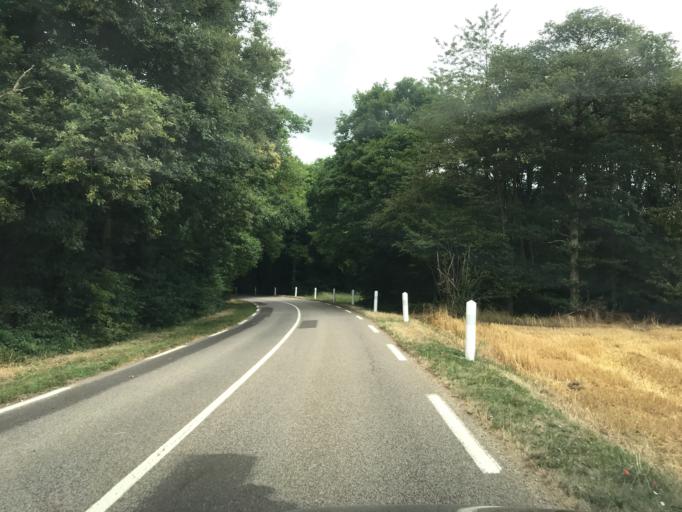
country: FR
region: Haute-Normandie
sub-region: Departement de l'Eure
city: Menilles
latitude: 49.0361
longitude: 1.2901
